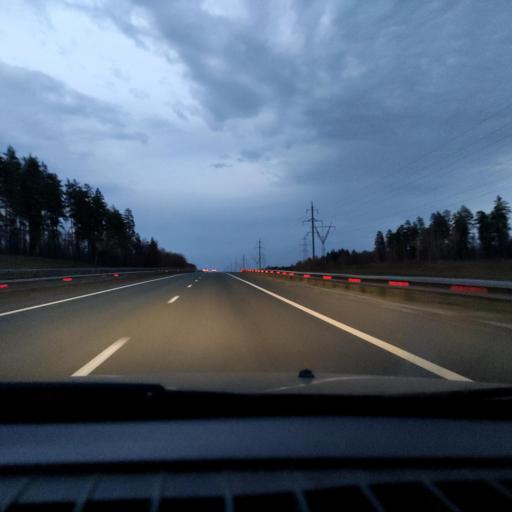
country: RU
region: Samara
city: Povolzhskiy
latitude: 53.5172
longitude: 49.7804
